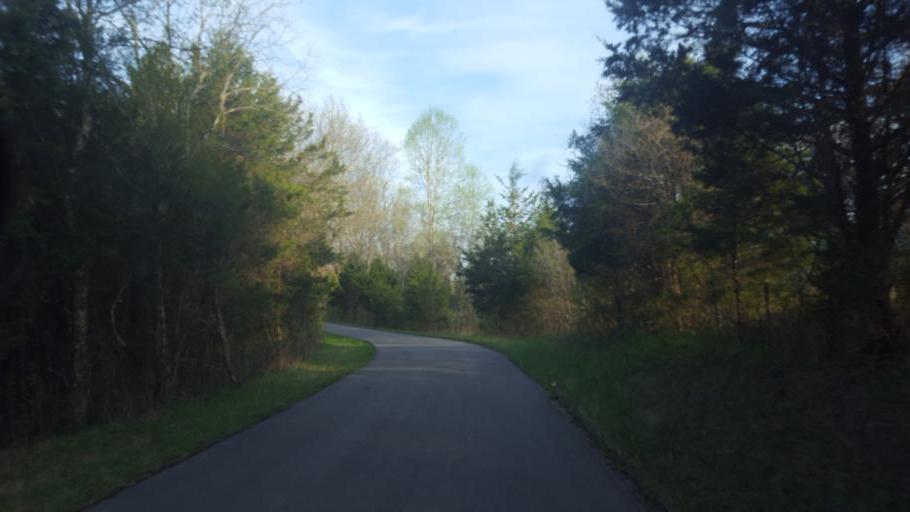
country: US
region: Kentucky
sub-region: Barren County
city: Cave City
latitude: 37.2024
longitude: -86.0194
